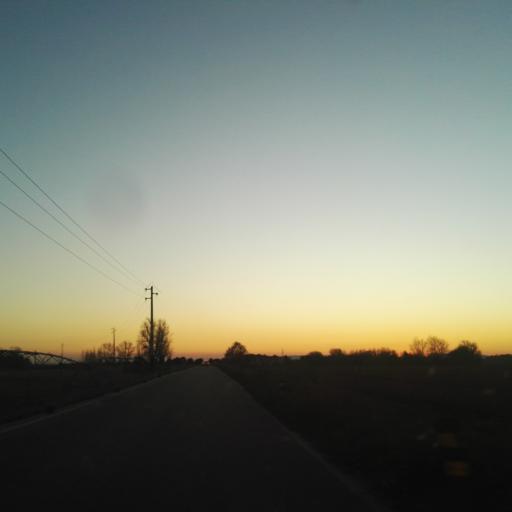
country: PT
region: Santarem
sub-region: Alpiarca
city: Alpiarca
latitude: 39.2998
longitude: -8.5786
